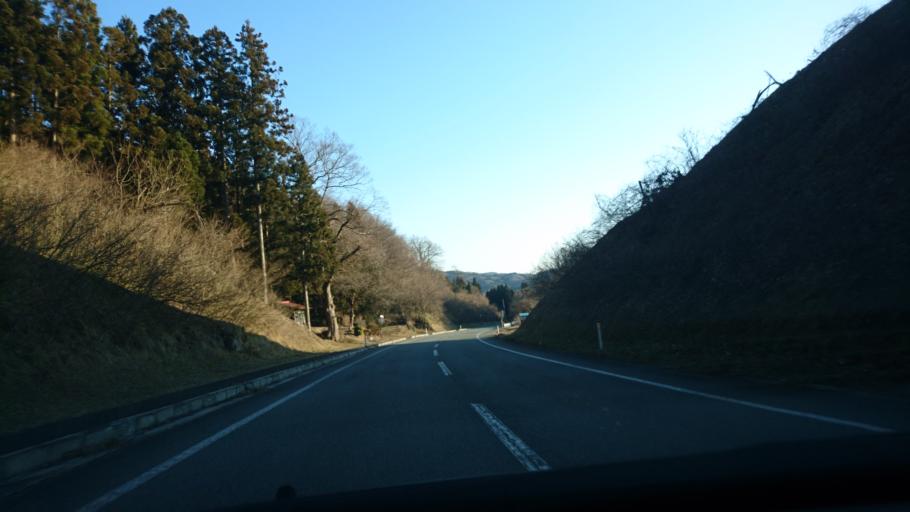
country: JP
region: Iwate
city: Ichinoseki
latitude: 39.0249
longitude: 141.3799
